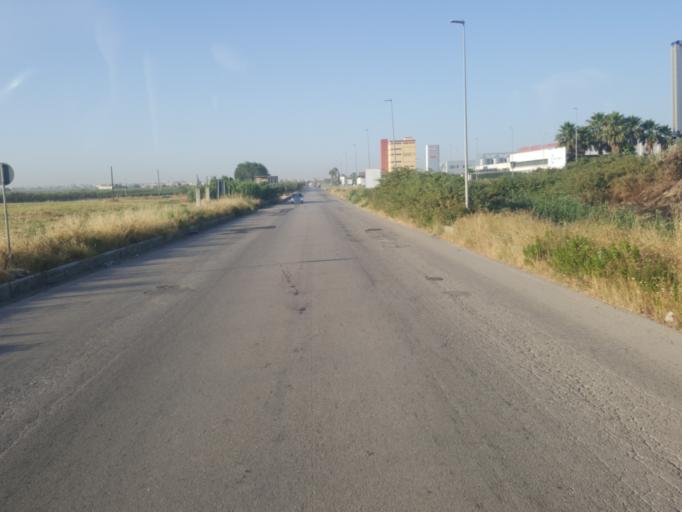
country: IT
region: Apulia
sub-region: Provincia di Foggia
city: Cerignola
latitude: 41.3043
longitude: 15.8984
